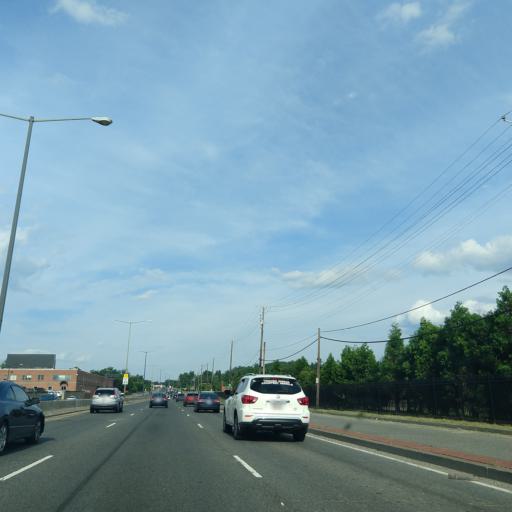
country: US
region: Maryland
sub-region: Prince George's County
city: Mount Rainier
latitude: 38.9173
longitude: -76.9689
